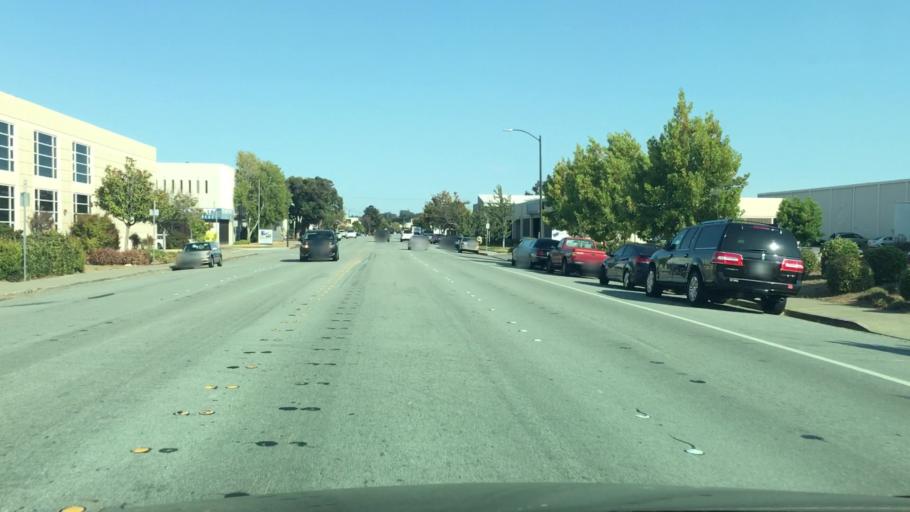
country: US
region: California
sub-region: San Mateo County
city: Burlingame
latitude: 37.5938
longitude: -122.3719
